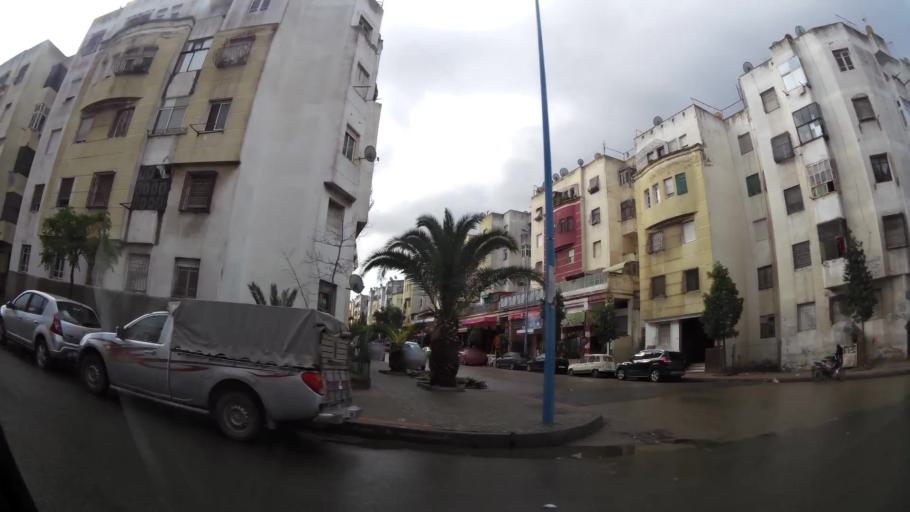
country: MA
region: Grand Casablanca
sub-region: Mediouna
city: Tit Mellil
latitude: 33.6002
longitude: -7.5351
